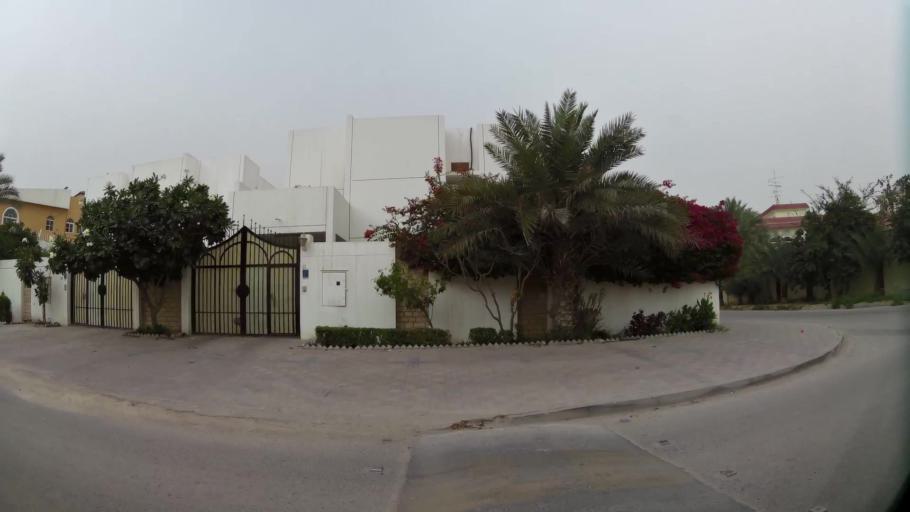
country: QA
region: Baladiyat ad Dawhah
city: Doha
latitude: 25.2571
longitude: 51.4913
